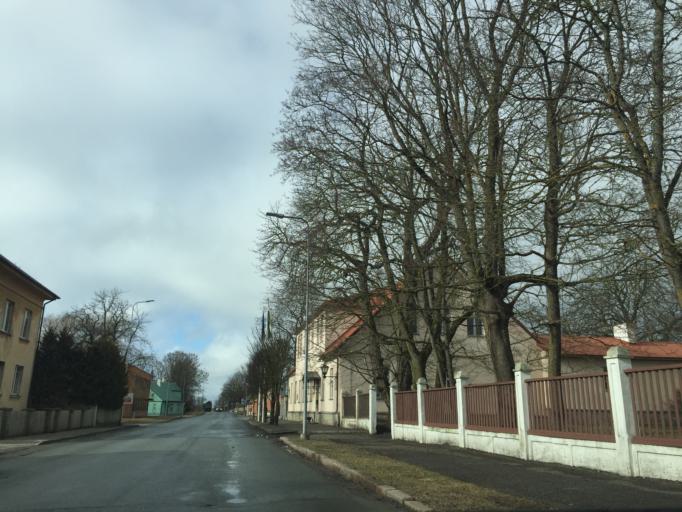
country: EE
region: Laeaene
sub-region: Haapsalu linn
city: Haapsalu
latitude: 58.9463
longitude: 23.5320
